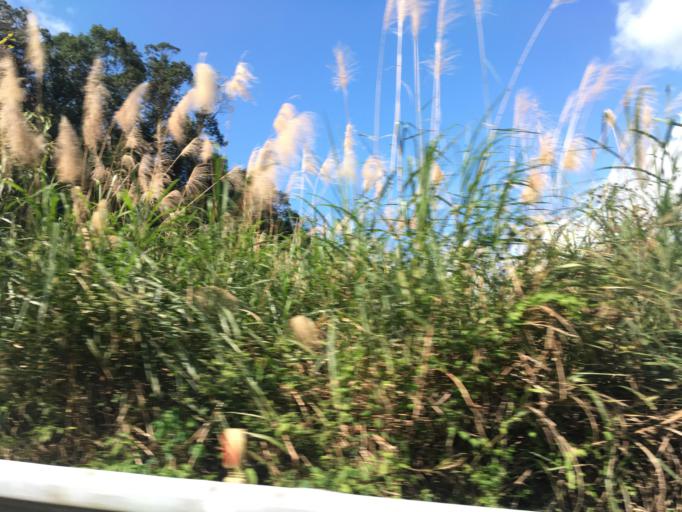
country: TW
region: Taiwan
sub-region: Yilan
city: Yilan
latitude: 24.7468
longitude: 121.6511
